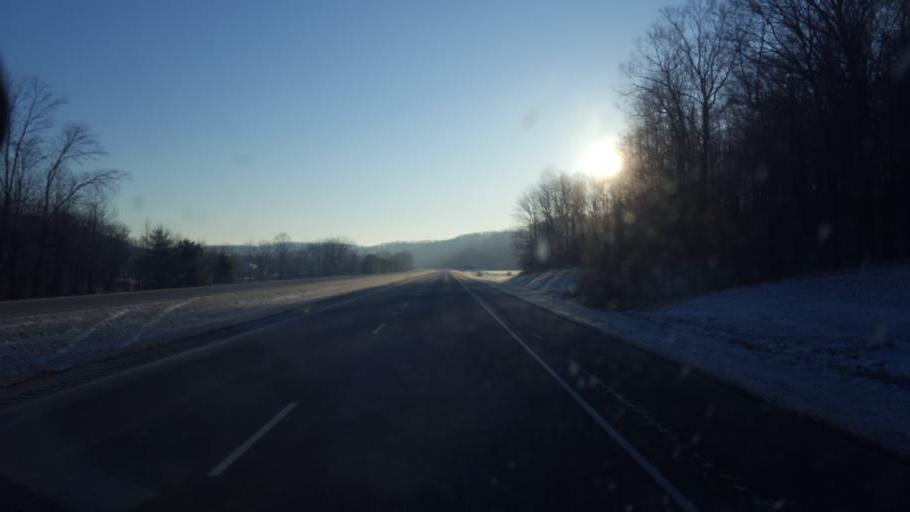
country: US
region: Ohio
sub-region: Pike County
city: Piketon
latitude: 39.0461
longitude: -83.1770
